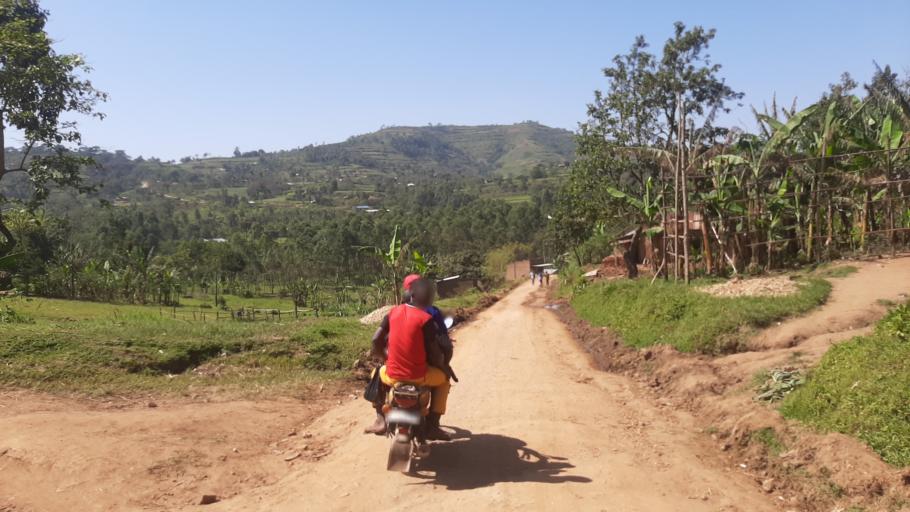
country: UG
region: Eastern Region
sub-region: Manafwa District
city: Manafwa
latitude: 0.9111
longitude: 34.3289
